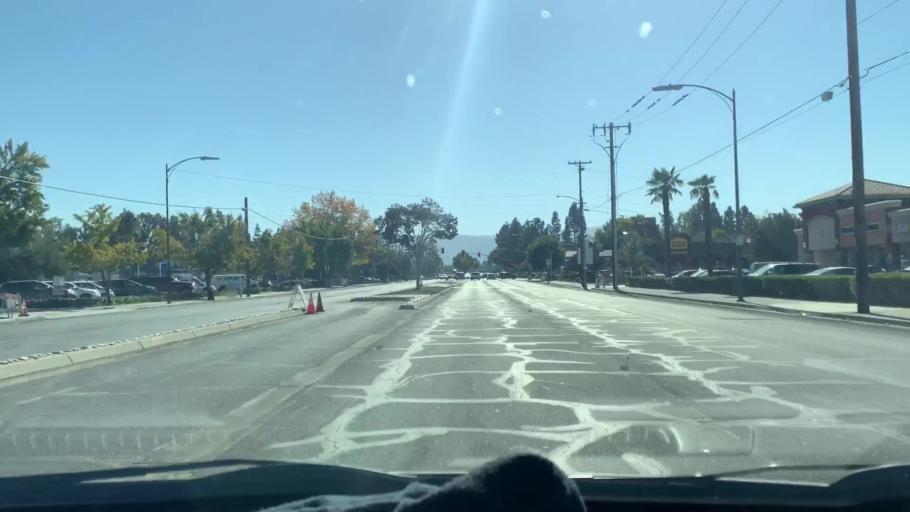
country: US
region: California
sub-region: Santa Clara County
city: Santa Clara
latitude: 37.3216
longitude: -121.9713
